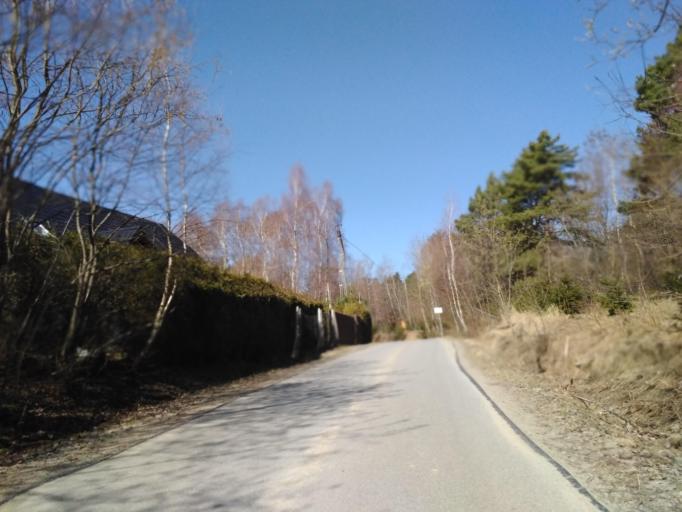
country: PL
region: Subcarpathian Voivodeship
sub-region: Powiat brzozowski
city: Jablonica Polska
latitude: 49.7312
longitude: 21.9063
